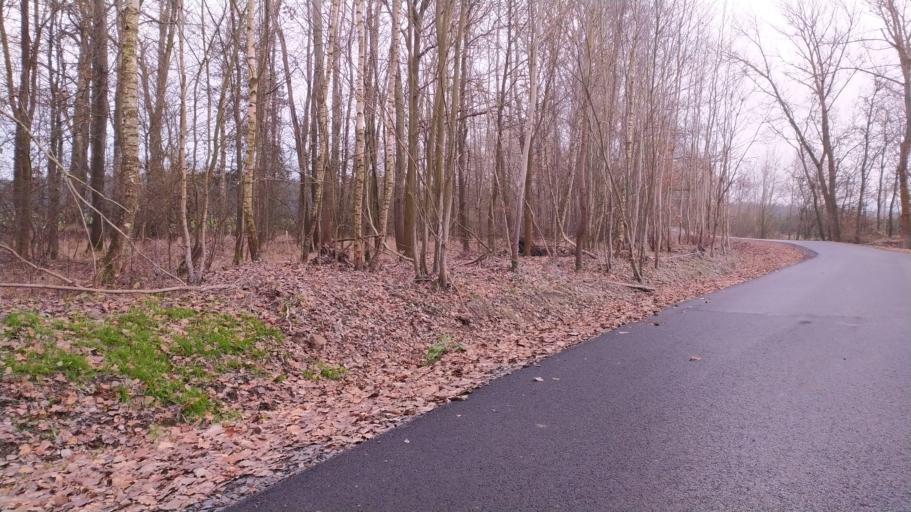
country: DE
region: Bavaria
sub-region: Upper Franconia
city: Schirnding
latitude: 50.1024
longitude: 12.2664
